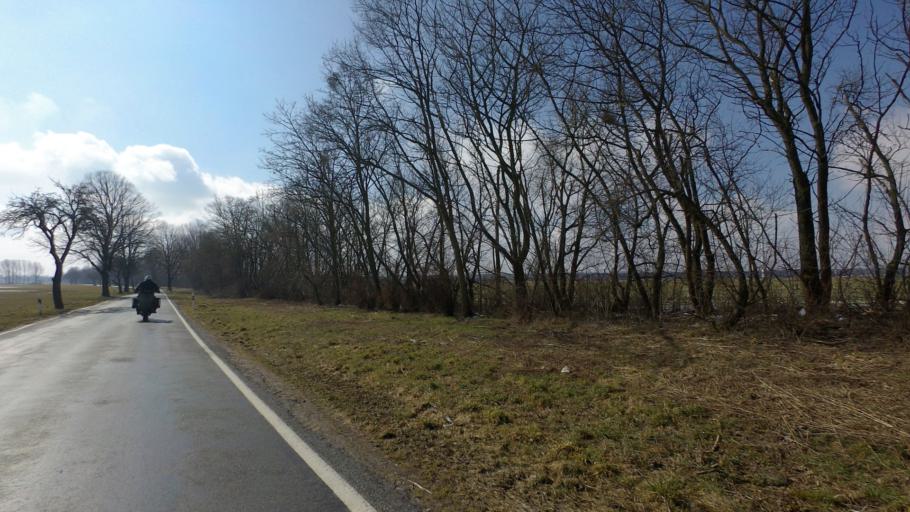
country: DE
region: Brandenburg
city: Werneuchen
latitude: 52.7006
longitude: 13.7206
